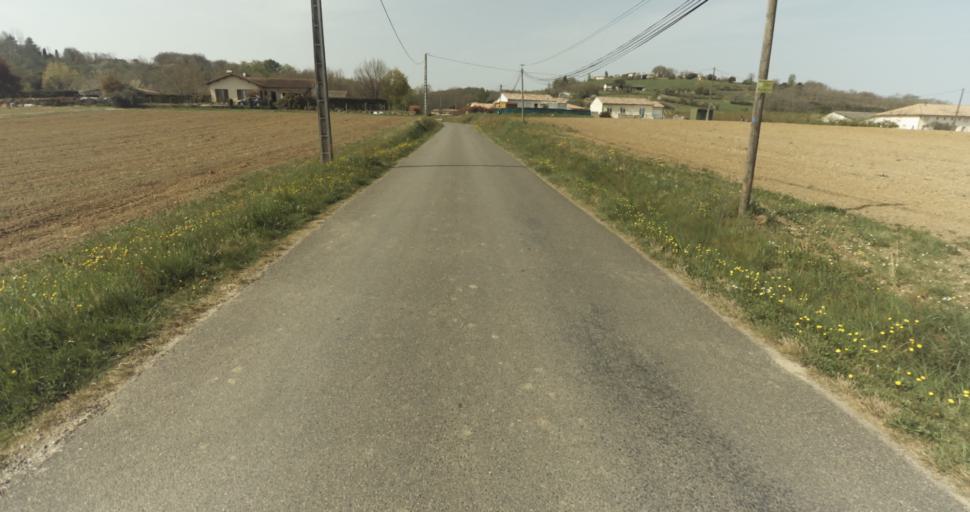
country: FR
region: Midi-Pyrenees
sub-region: Departement du Tarn-et-Garonne
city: Moissac
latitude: 44.1260
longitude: 1.1514
